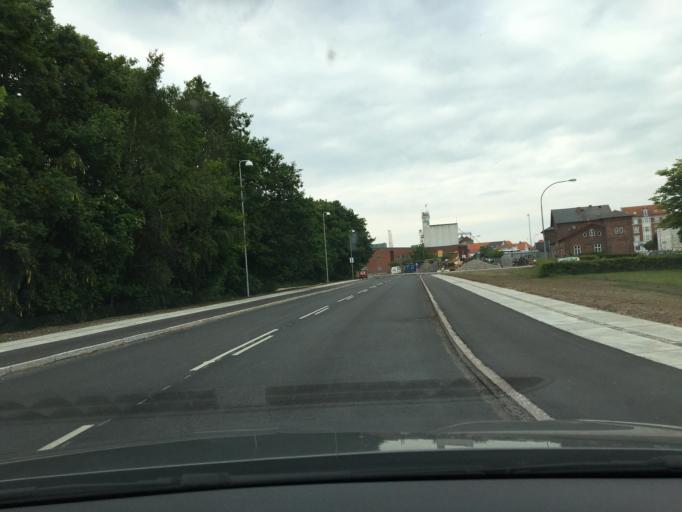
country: DK
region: South Denmark
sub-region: Assens Kommune
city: Assens
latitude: 55.2679
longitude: 9.8915
